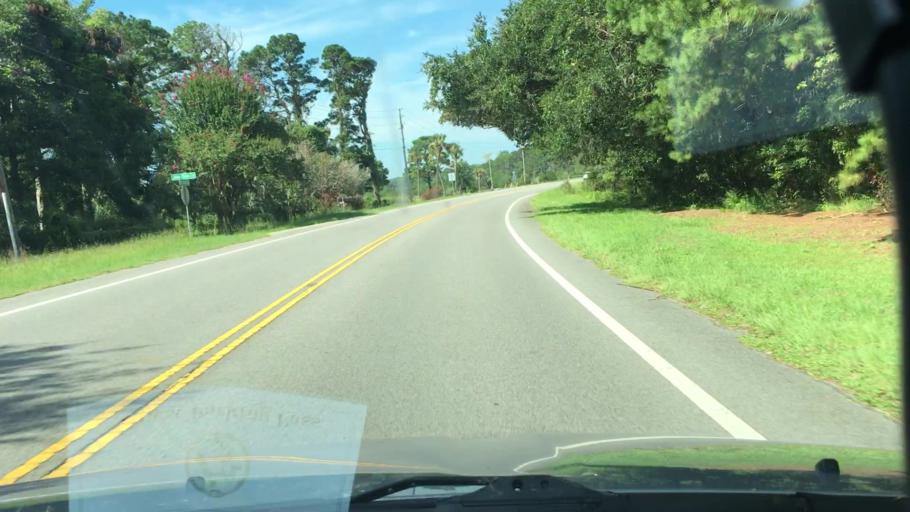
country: US
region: South Carolina
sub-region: Beaufort County
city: Beaufort
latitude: 32.4004
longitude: -80.5382
